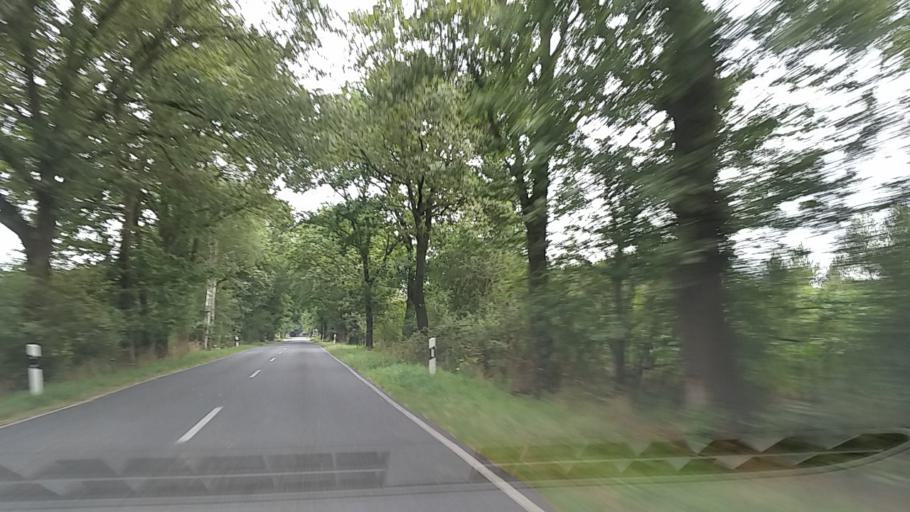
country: DE
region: Lower Saxony
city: Vollersode
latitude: 53.4091
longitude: 8.9171
